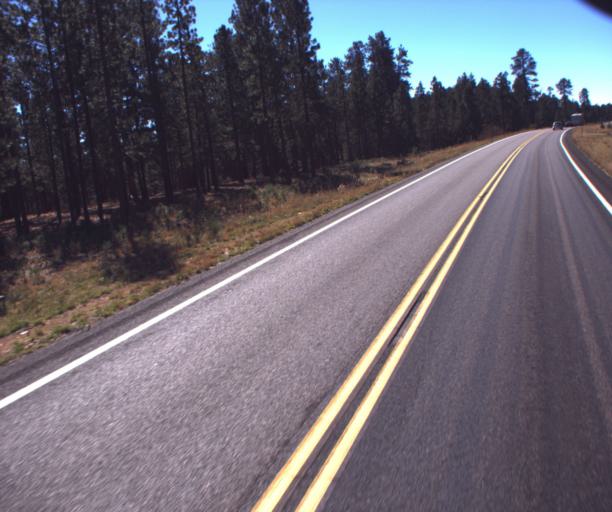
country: US
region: Arizona
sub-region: Coconino County
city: Fredonia
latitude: 36.6929
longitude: -112.2147
